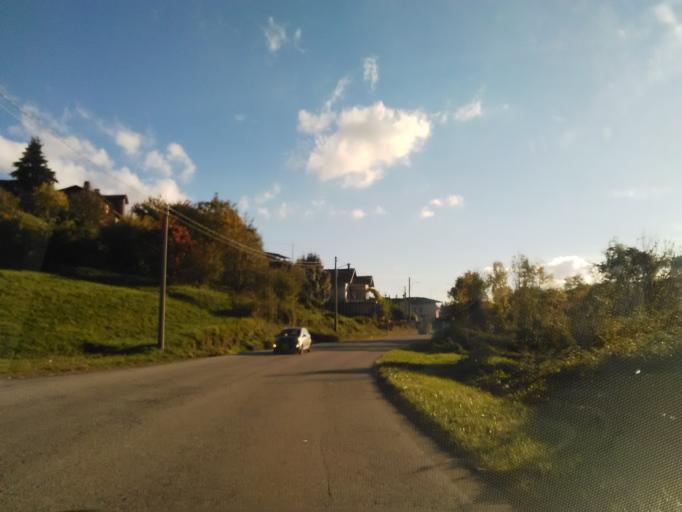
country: IT
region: Piedmont
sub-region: Provincia di Biella
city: Sostegno
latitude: 45.6572
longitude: 8.2684
